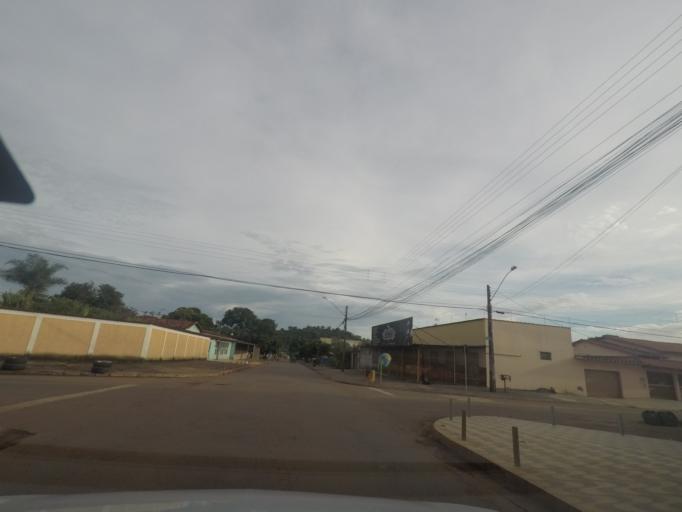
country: BR
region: Goias
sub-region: Goiania
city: Goiania
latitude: -16.6899
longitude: -49.3586
